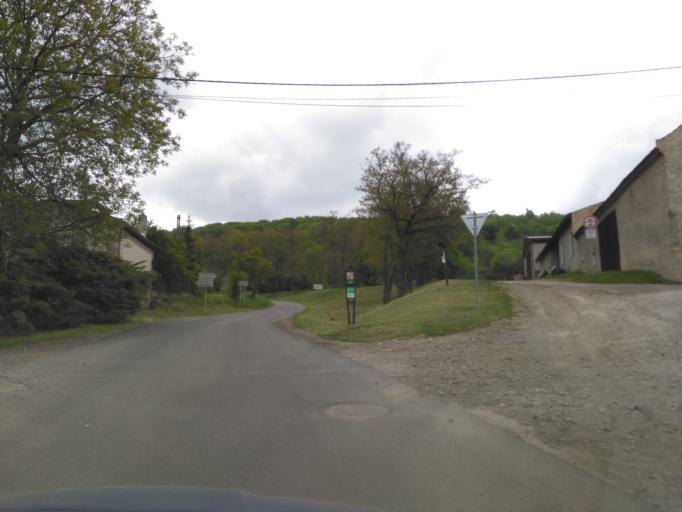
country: CZ
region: Central Bohemia
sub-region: Okres Beroun
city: Kraluv Dvur
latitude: 49.9206
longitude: 14.0660
